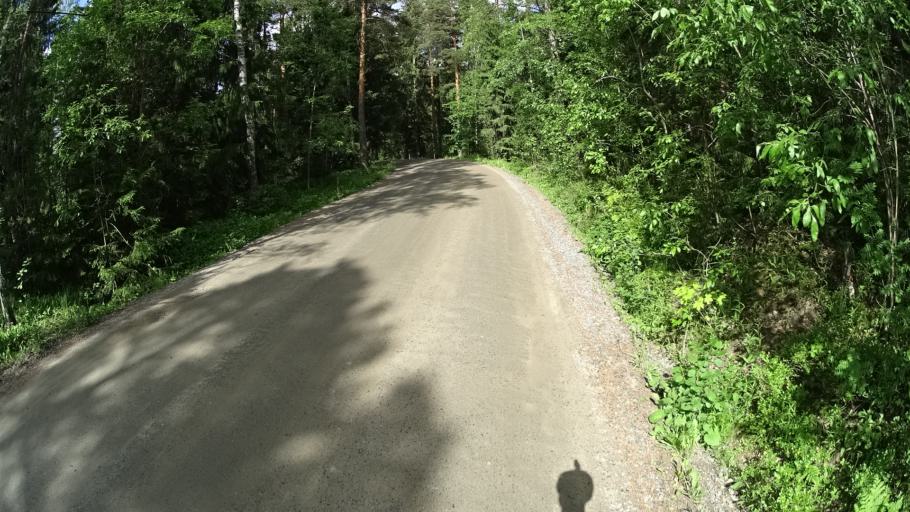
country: FI
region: Uusimaa
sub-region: Helsinki
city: Sibbo
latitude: 60.2861
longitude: 25.3121
